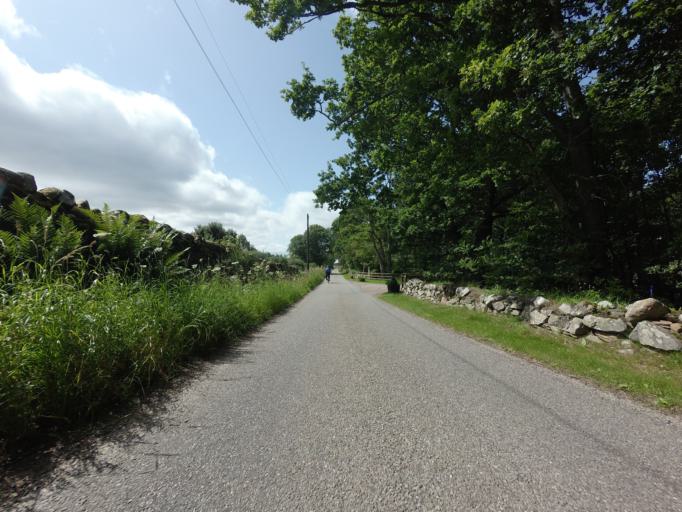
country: GB
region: Scotland
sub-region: Highland
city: Fortrose
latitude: 57.4930
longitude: -4.0101
